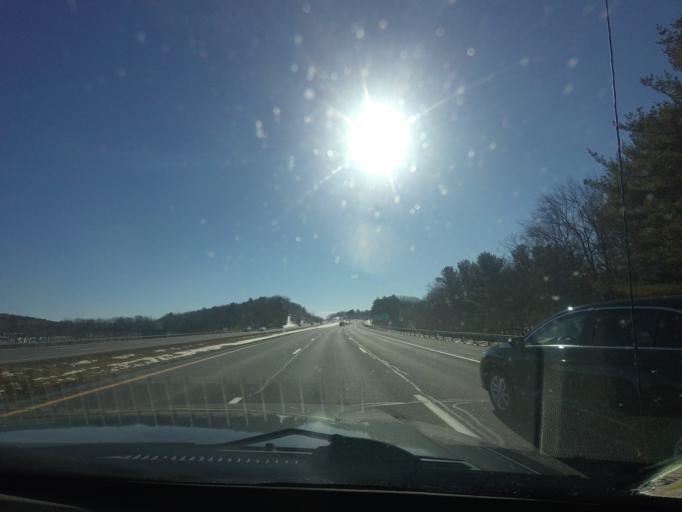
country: US
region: New York
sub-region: Rensselaer County
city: East Greenbush
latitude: 42.5862
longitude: -73.6773
